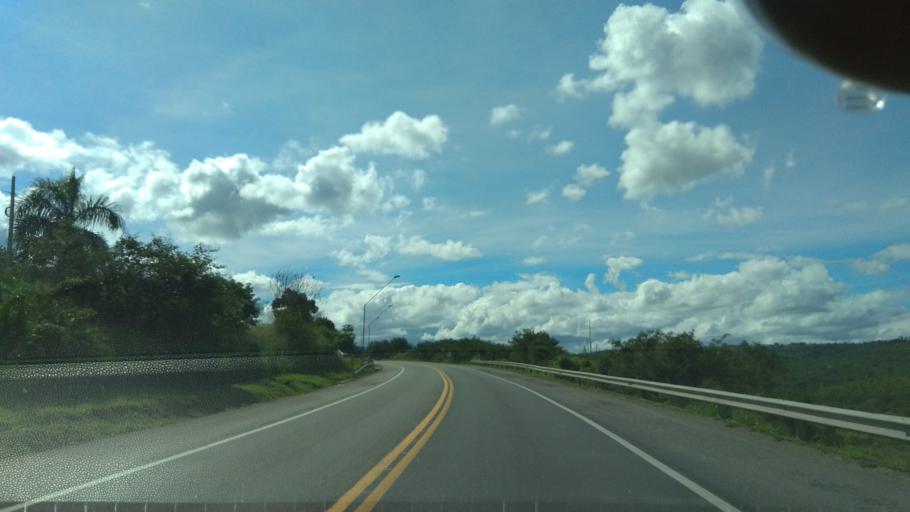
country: BR
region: Bahia
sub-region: Santa Ines
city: Santa Ines
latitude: -13.2318
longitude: -40.0170
